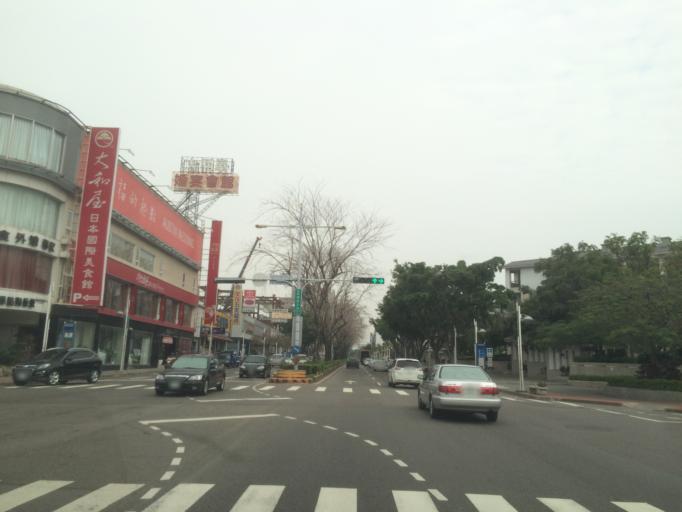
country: TW
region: Taiwan
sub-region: Taichung City
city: Taichung
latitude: 24.1902
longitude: 120.6864
